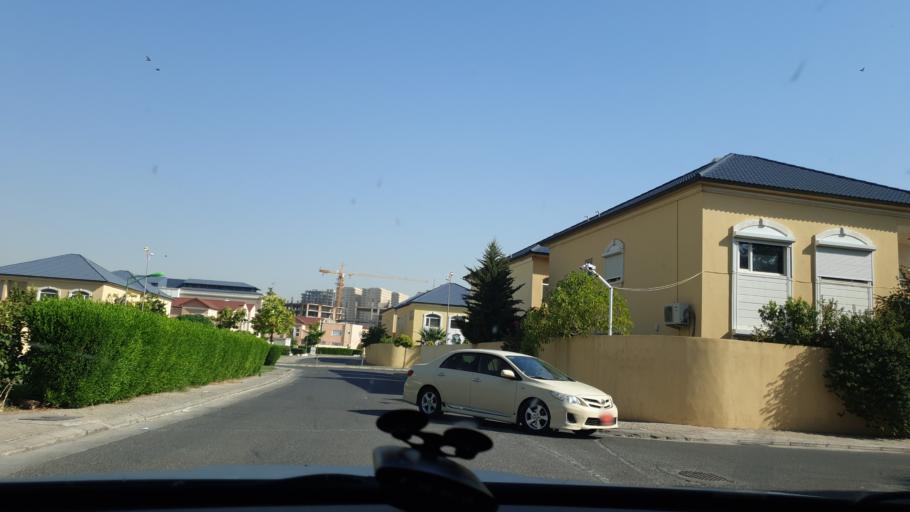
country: IQ
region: Arbil
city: Erbil
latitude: 36.1867
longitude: 43.9667
